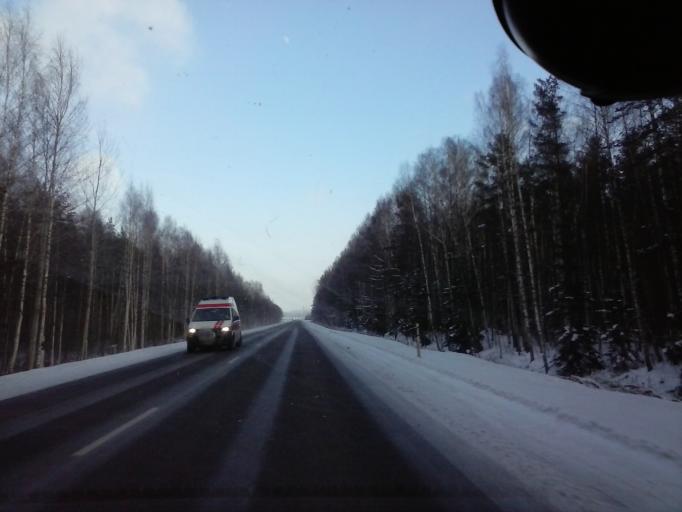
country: EE
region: Tartu
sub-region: Puhja vald
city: Puhja
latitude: 58.3268
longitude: 26.2494
